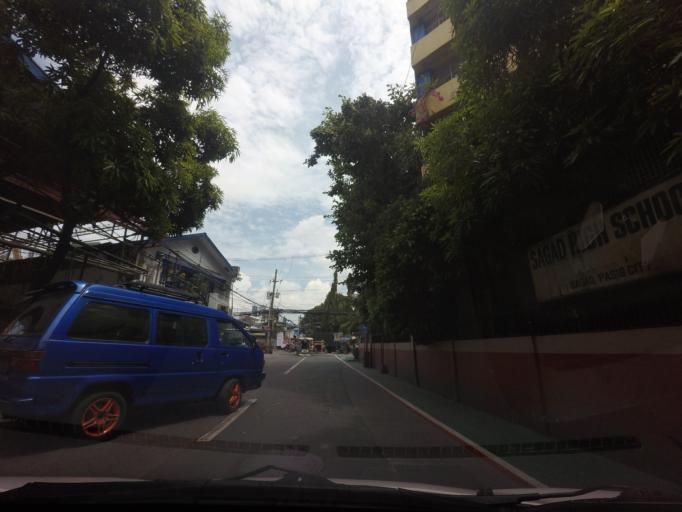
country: PH
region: Metro Manila
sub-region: Pasig
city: Pasig City
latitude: 14.5665
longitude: 121.0796
